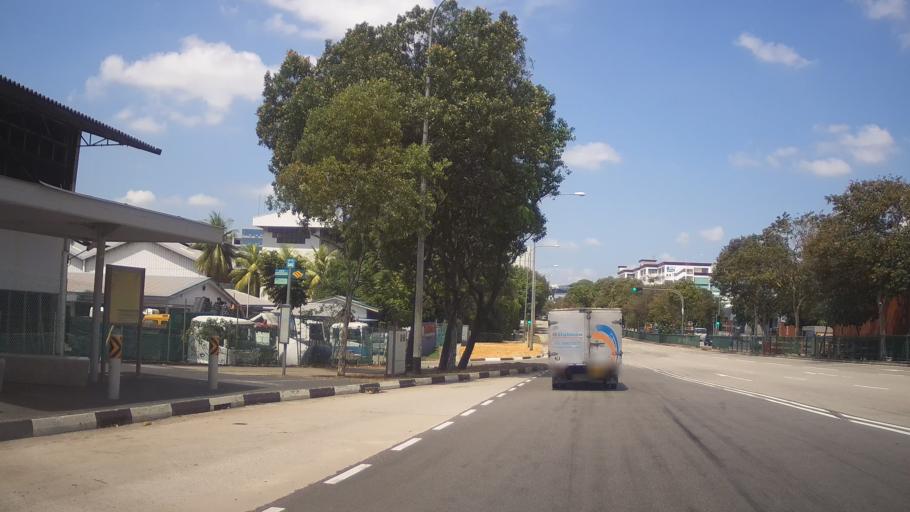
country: SG
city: Singapore
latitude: 1.3140
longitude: 103.7084
